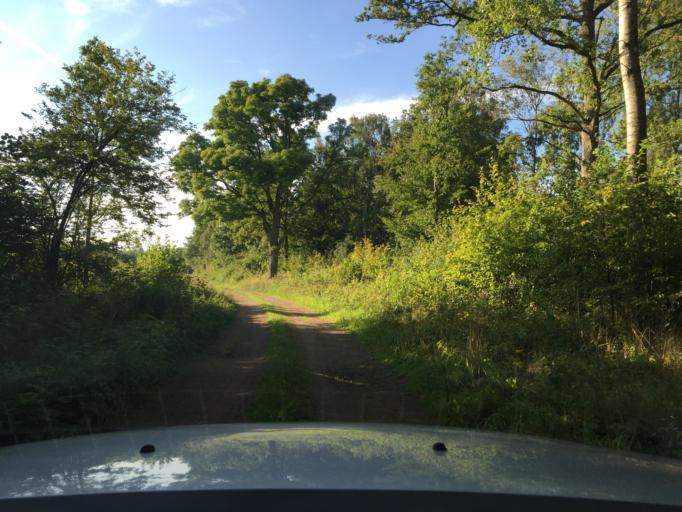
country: SE
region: Skane
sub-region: Hassleholms Kommun
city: Sosdala
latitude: 56.0240
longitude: 13.7082
